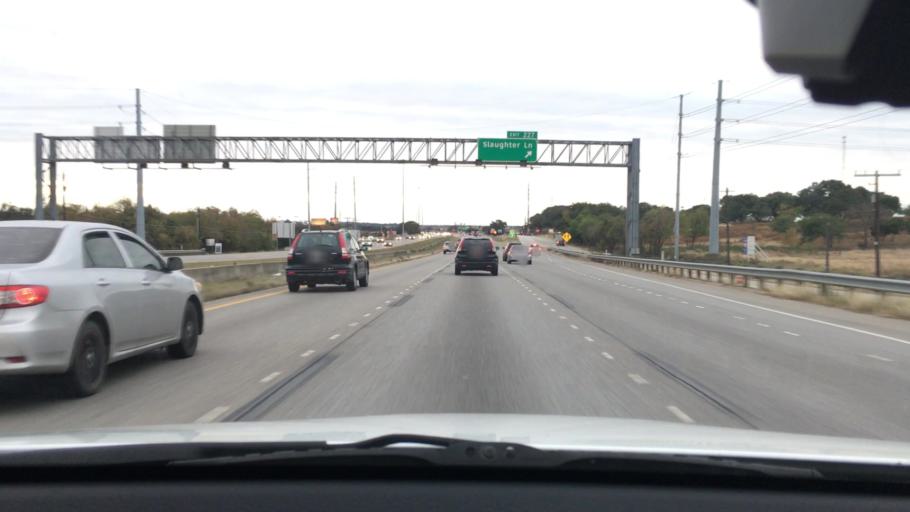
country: US
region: Texas
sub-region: Travis County
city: Onion Creek
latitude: 30.1733
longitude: -97.7822
